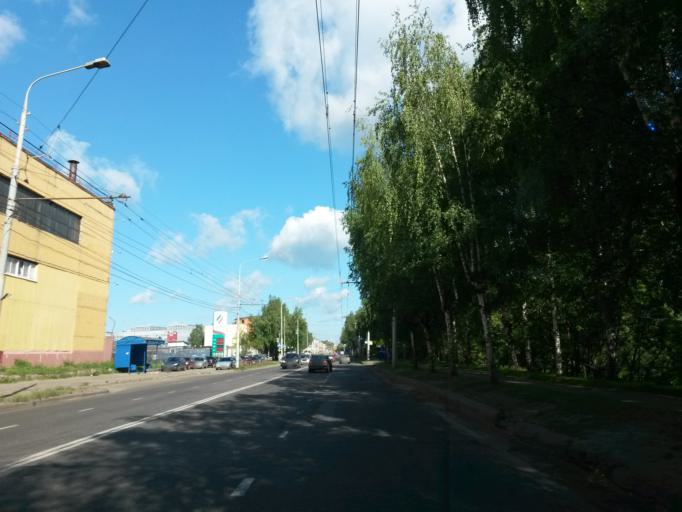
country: RU
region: Jaroslavl
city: Yaroslavl
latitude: 57.6526
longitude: 39.8735
